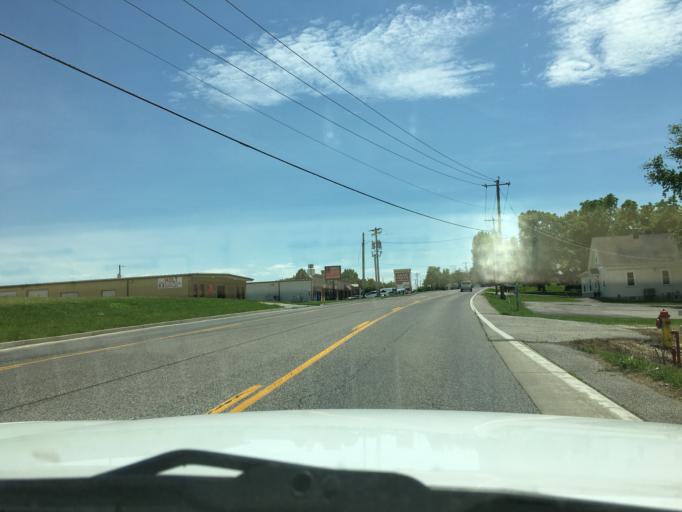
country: US
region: Missouri
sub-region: Franklin County
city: Washington
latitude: 38.5411
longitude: -91.0179
